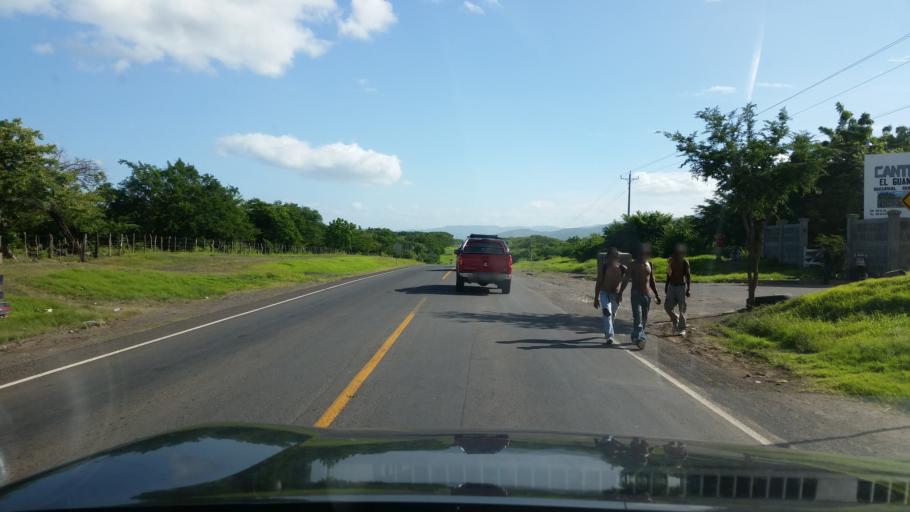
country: NI
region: Managua
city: Tipitapa
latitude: 12.3617
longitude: -86.0481
